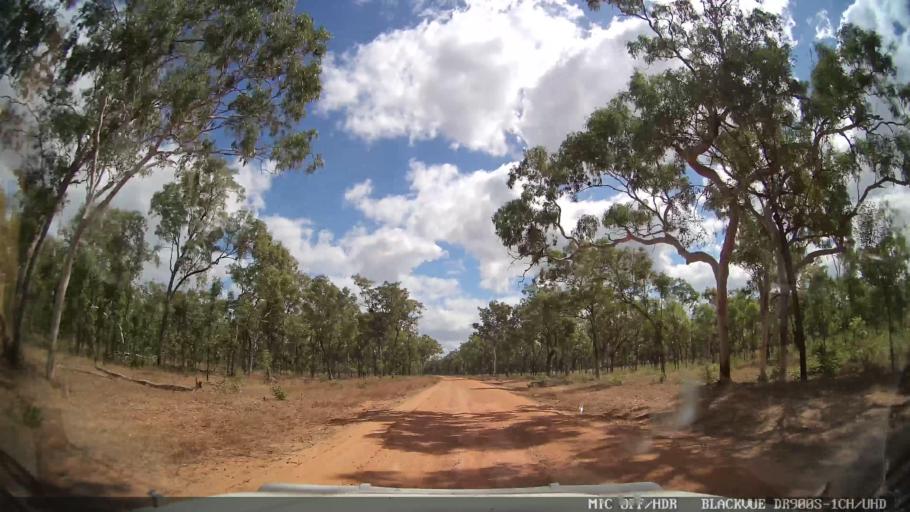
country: AU
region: Queensland
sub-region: Cook
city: Cooktown
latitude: -15.3515
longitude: 144.4671
